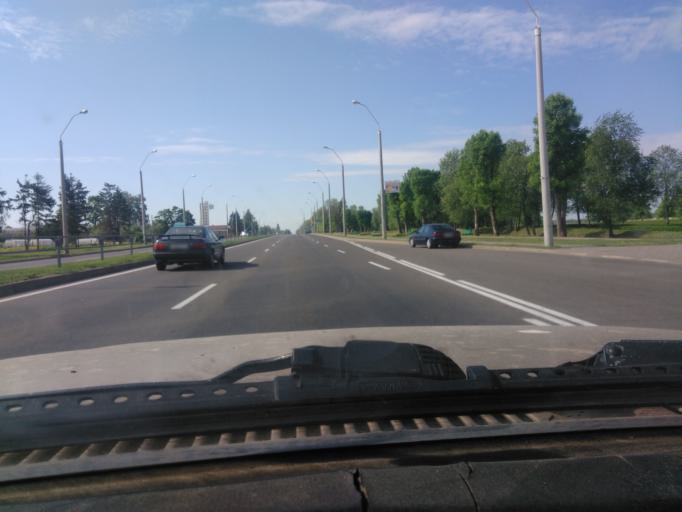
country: BY
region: Mogilev
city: Buynichy
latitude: 53.8616
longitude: 30.2582
